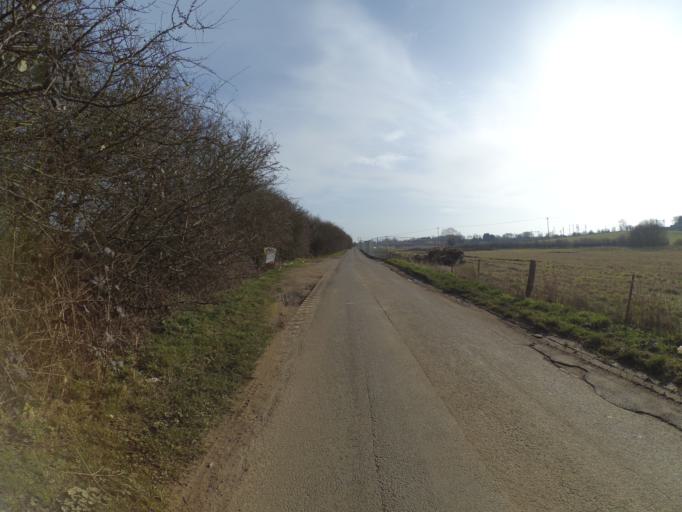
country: GB
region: England
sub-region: Warwickshire
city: Rugby
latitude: 52.3606
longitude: -1.2009
